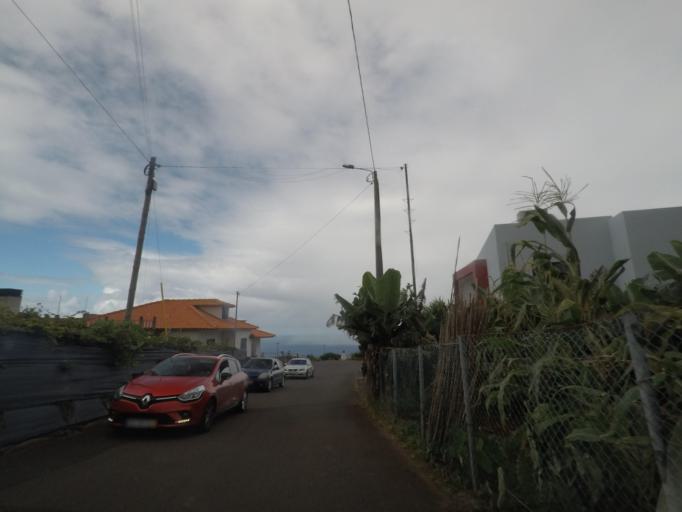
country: PT
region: Madeira
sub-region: Santana
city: Santana
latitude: 32.8337
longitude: -16.9118
